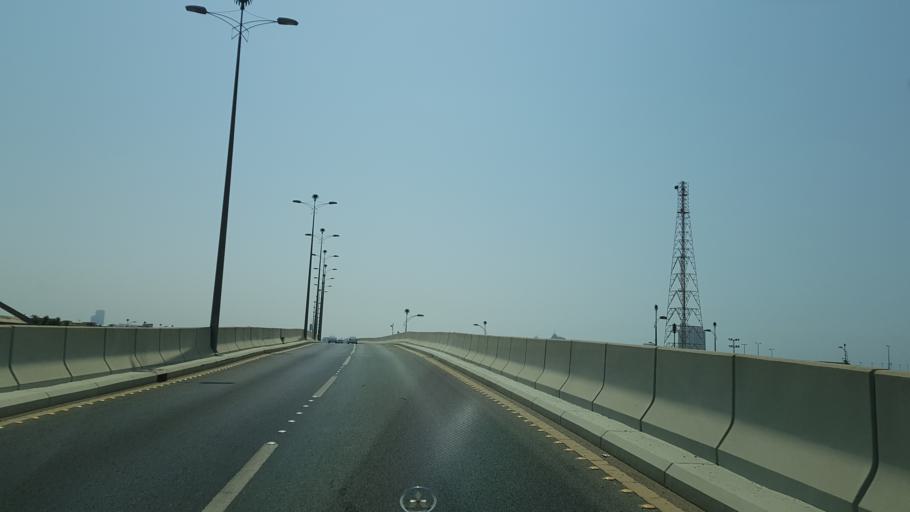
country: SA
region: Makkah
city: Jeddah
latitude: 21.5422
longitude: 39.1551
